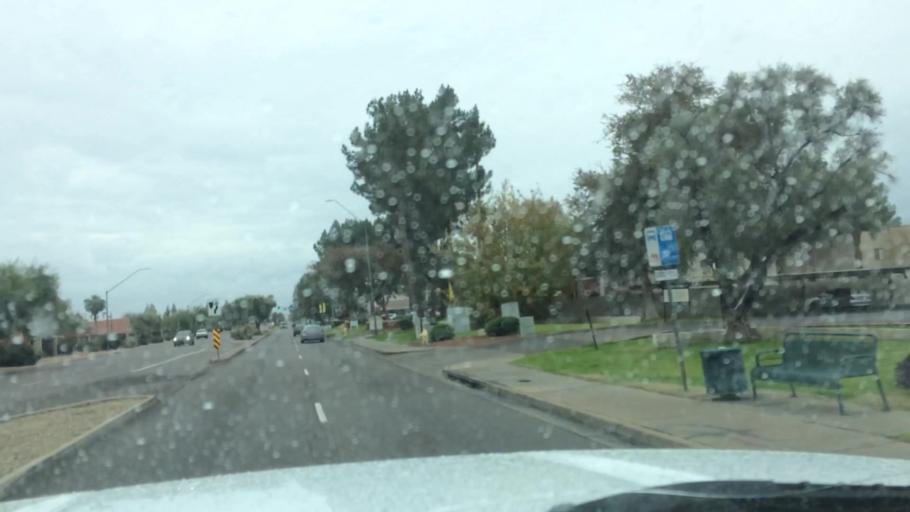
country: US
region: Arizona
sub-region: Maricopa County
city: Peoria
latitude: 33.6231
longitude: -112.1858
